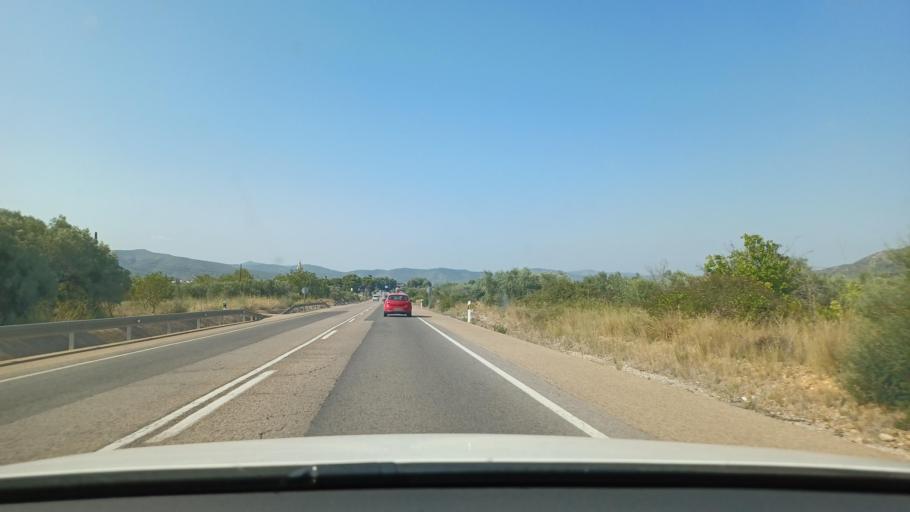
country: ES
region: Valencia
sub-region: Provincia de Castello
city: Alcala de Xivert
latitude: 40.2901
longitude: 0.2255
